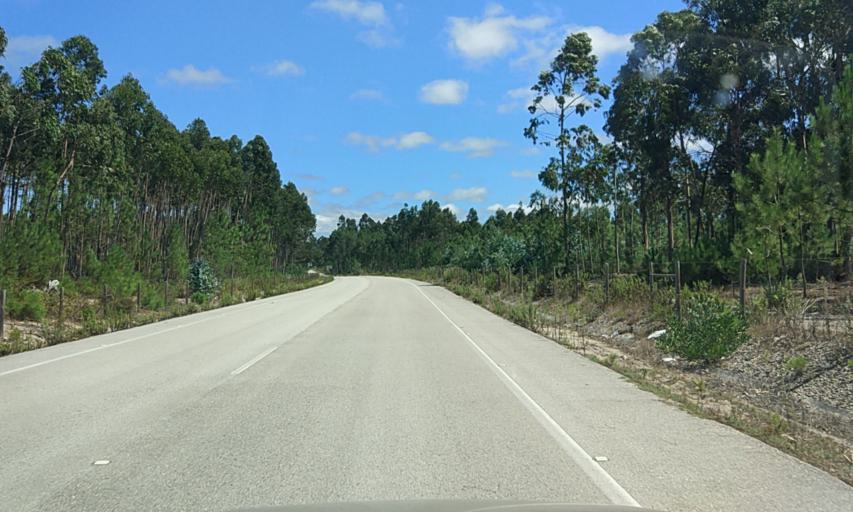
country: PT
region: Coimbra
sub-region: Mira
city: Mira
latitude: 40.3377
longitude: -8.7399
